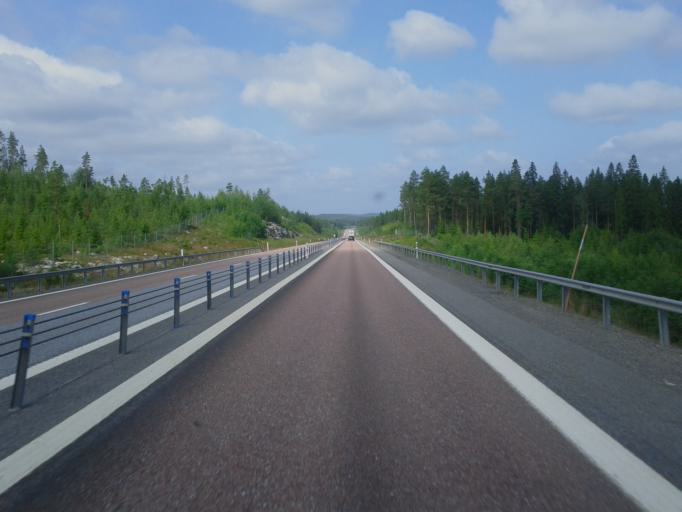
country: SE
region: Vaesterbotten
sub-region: Skelleftea Kommun
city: Soedra Bergsbyn
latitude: 64.6892
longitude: 21.0451
